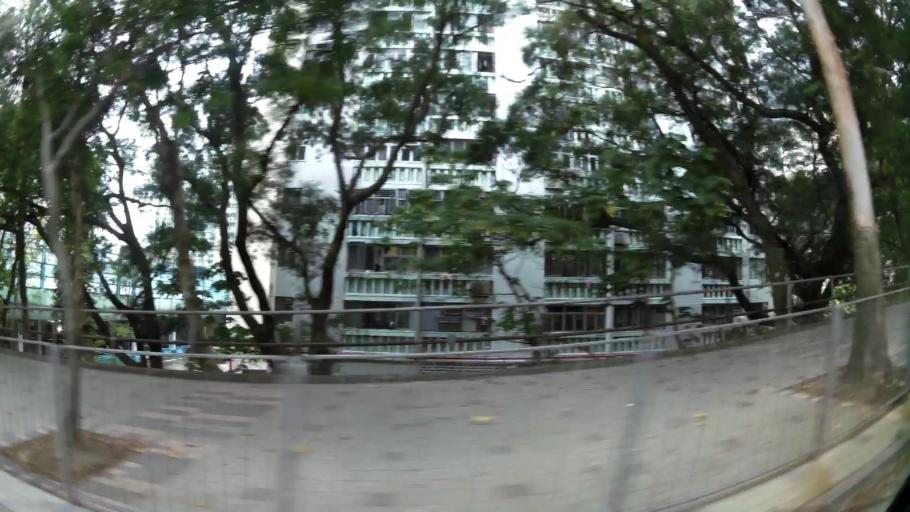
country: HK
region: Kowloon City
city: Kowloon
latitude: 22.3329
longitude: 114.2175
